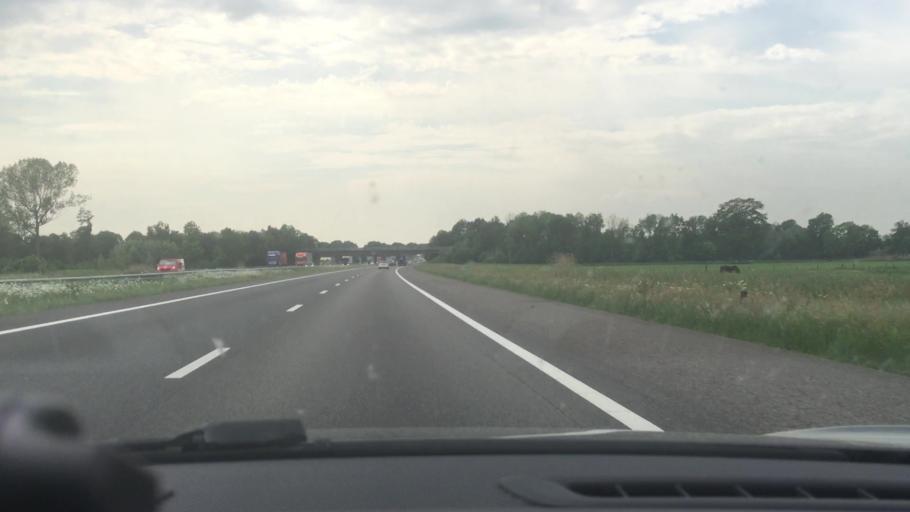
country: NL
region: Overijssel
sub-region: Gemeente Hof van Twente
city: Goor
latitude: 52.2846
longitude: 6.5938
